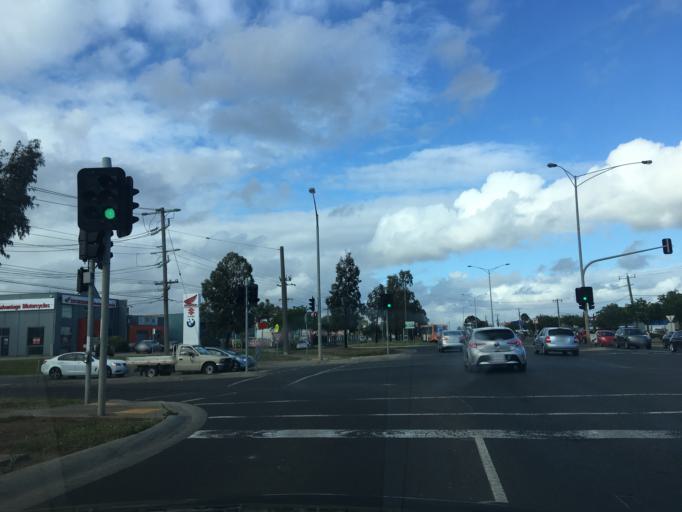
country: AU
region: Victoria
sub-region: Wyndham
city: Williams Landing
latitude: -37.8720
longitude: 144.7250
